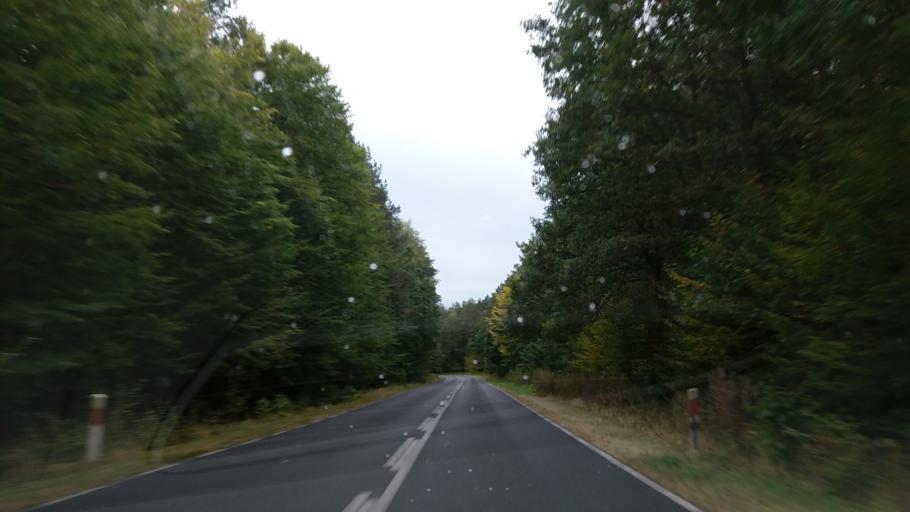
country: PL
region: West Pomeranian Voivodeship
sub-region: Powiat mysliborski
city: Barlinek
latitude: 52.9059
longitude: 15.1925
